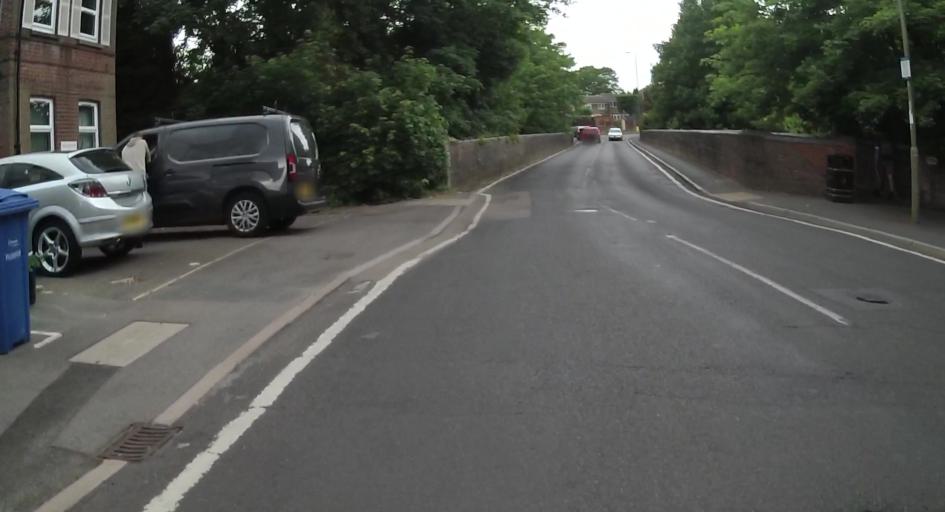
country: GB
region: England
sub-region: Hampshire
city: Aldershot
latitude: 51.2433
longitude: -0.7637
